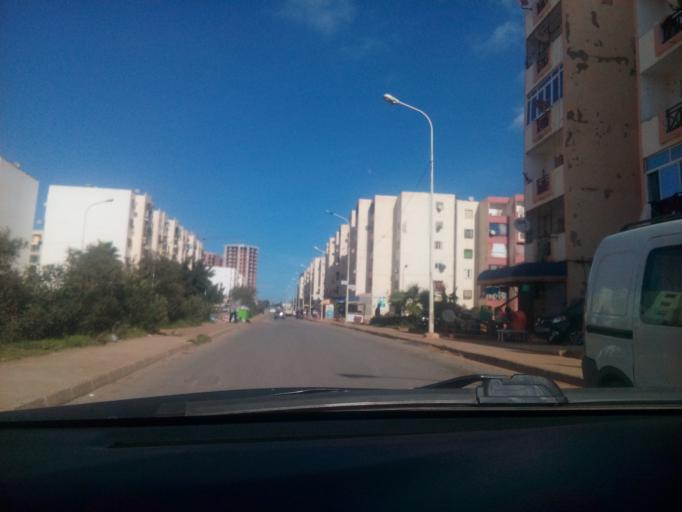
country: DZ
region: Oran
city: Bir el Djir
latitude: 35.7047
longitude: -0.5637
